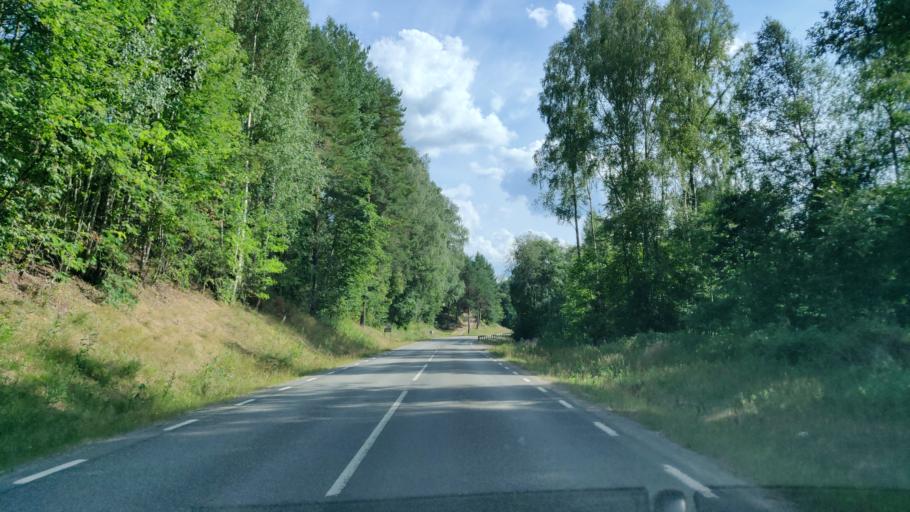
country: SE
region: Vaermland
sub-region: Hagfors Kommun
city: Ekshaerad
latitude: 60.1743
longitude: 13.5293
